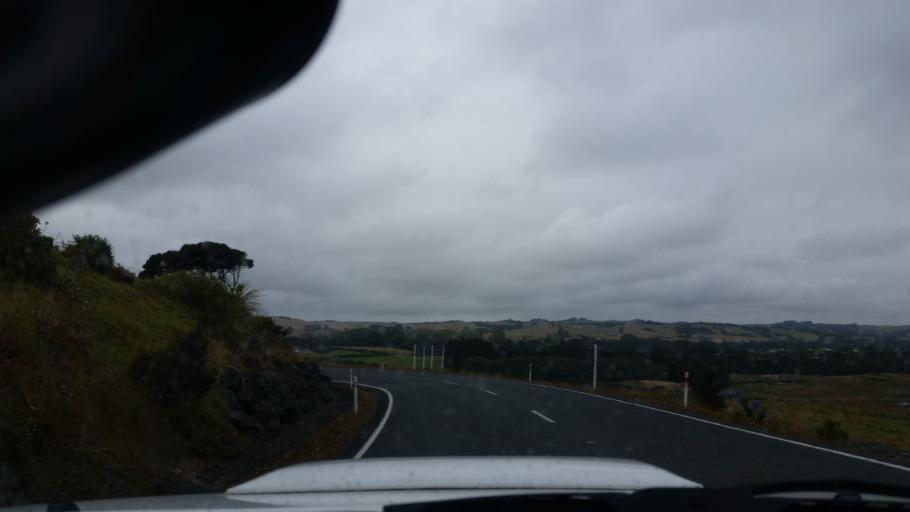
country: NZ
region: Auckland
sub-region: Auckland
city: Wellsford
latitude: -36.1444
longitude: 174.4967
